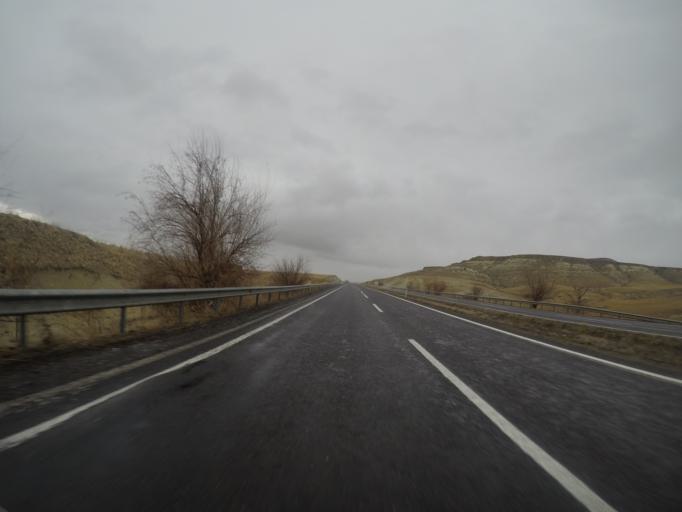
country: TR
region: Nevsehir
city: Urgub
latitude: 38.7359
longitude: 34.9799
